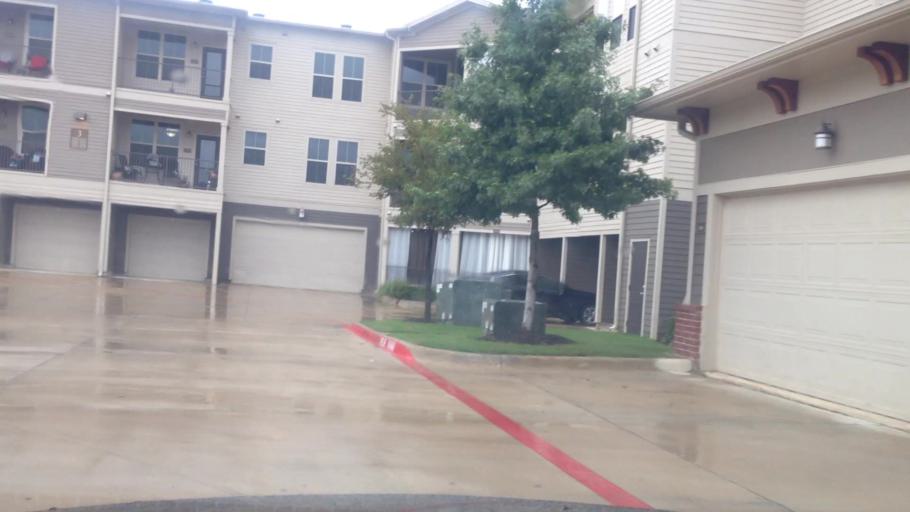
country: US
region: Texas
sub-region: Tarrant County
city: North Richland Hills
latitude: 32.8611
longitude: -97.1987
